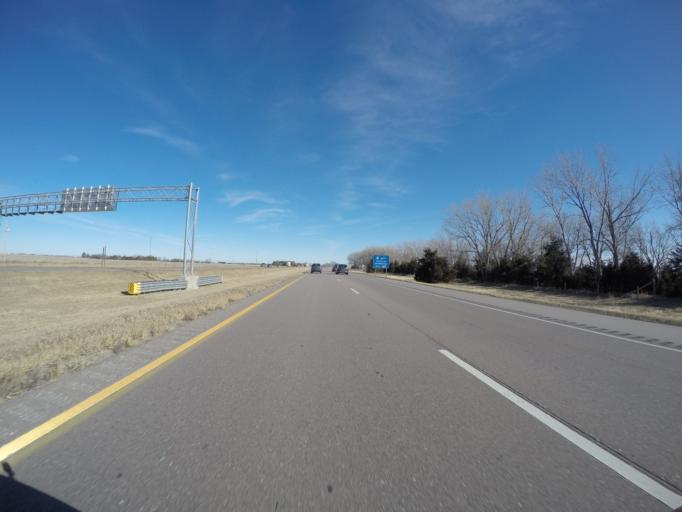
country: US
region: Nebraska
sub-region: York County
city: York
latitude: 40.8219
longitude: -97.5683
